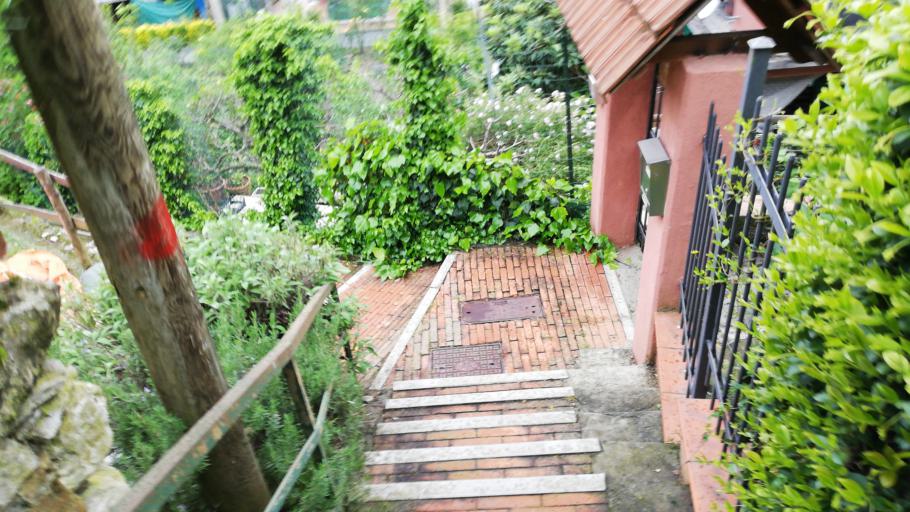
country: IT
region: Liguria
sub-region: Provincia di Genova
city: Piccarello
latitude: 44.4519
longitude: 9.0086
